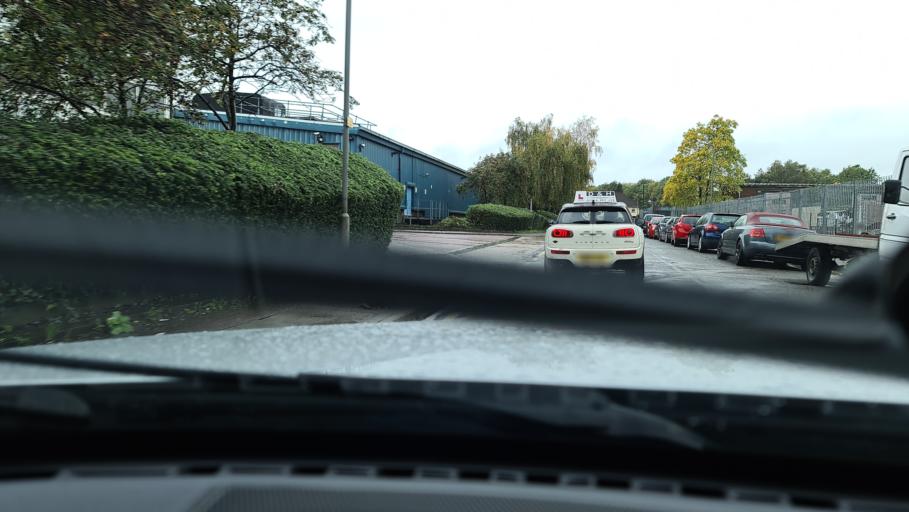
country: GB
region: England
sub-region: Buckinghamshire
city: Bletchley
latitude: 51.9994
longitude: -0.7266
